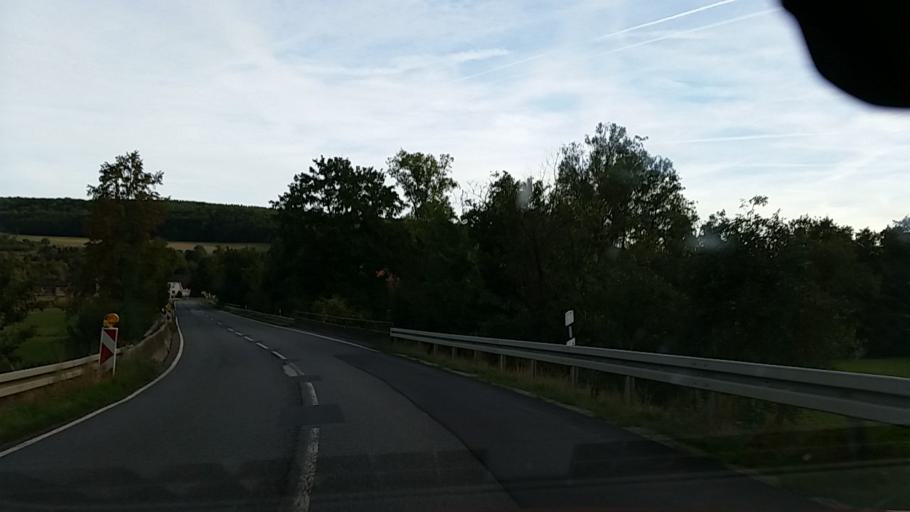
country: DE
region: Bavaria
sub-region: Regierungsbezirk Unterfranken
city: Thungen
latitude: 49.9545
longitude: 9.8873
